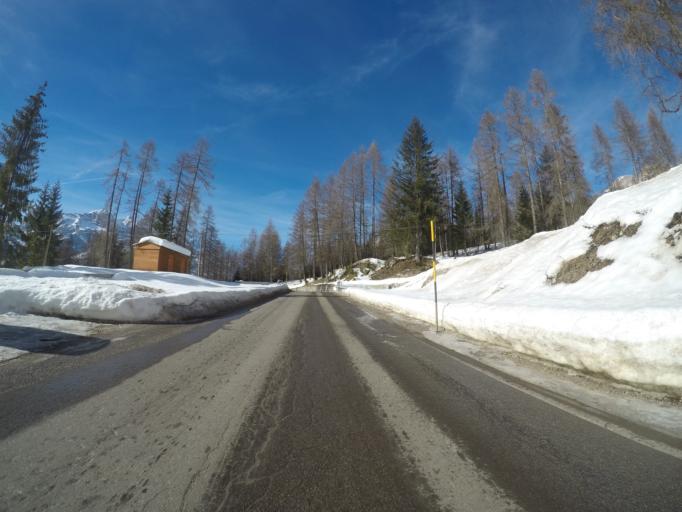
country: IT
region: Veneto
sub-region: Provincia di Belluno
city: Cortina d'Ampezzo
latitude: 46.5454
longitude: 12.1661
